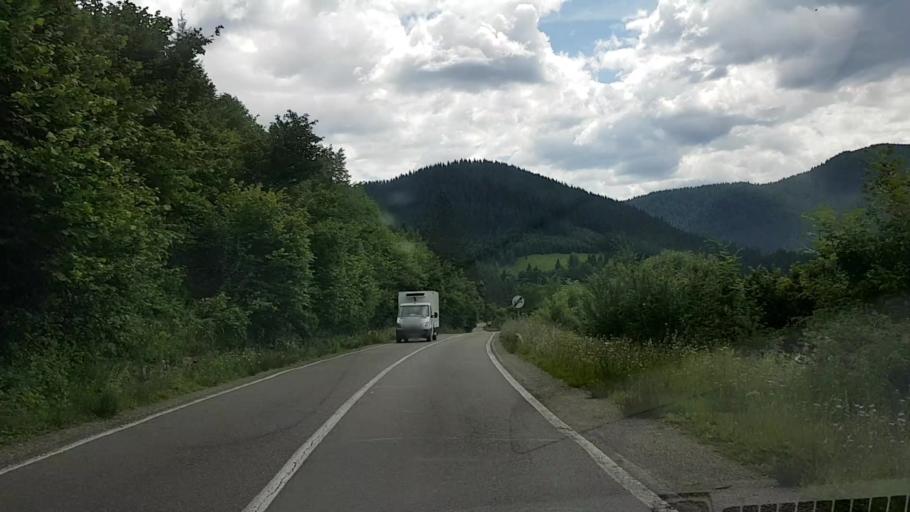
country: RO
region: Suceava
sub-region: Comuna Brosteni
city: Brosteni
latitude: 47.2346
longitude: 25.7432
